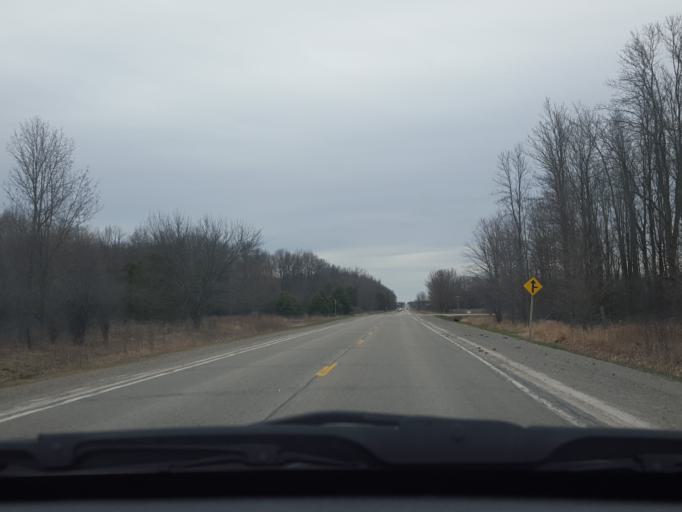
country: CA
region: Ontario
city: Uxbridge
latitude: 44.2930
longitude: -79.1693
